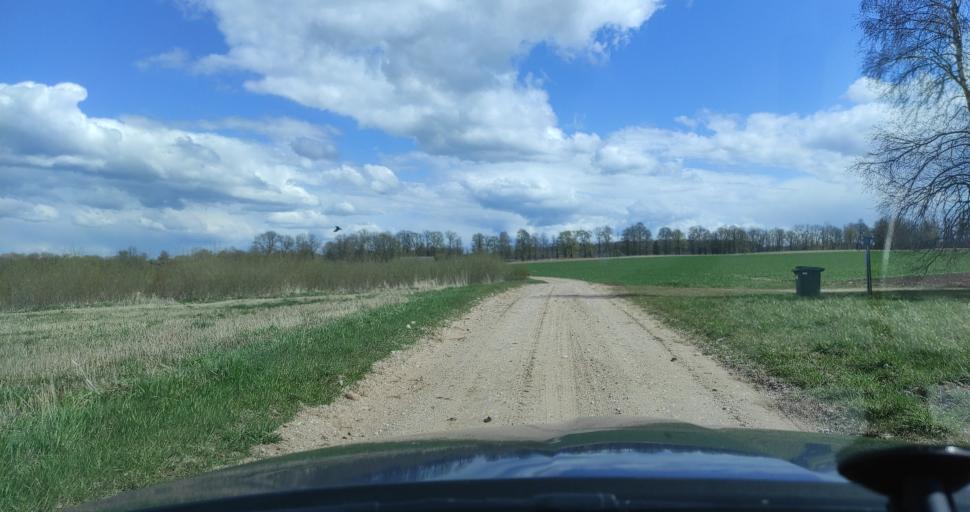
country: LV
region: Kuldigas Rajons
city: Kuldiga
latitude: 56.8629
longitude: 21.8061
